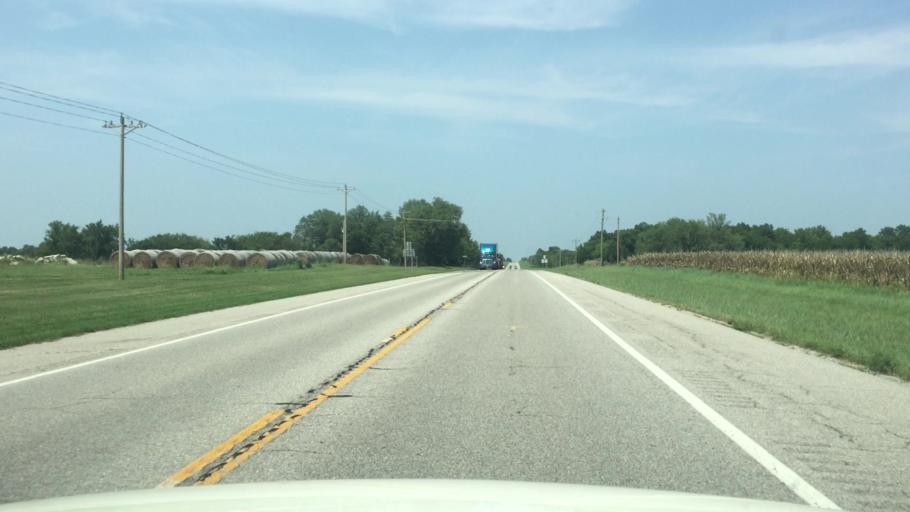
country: US
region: Missouri
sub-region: Jasper County
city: Carl Junction
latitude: 37.2498
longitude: -94.7051
